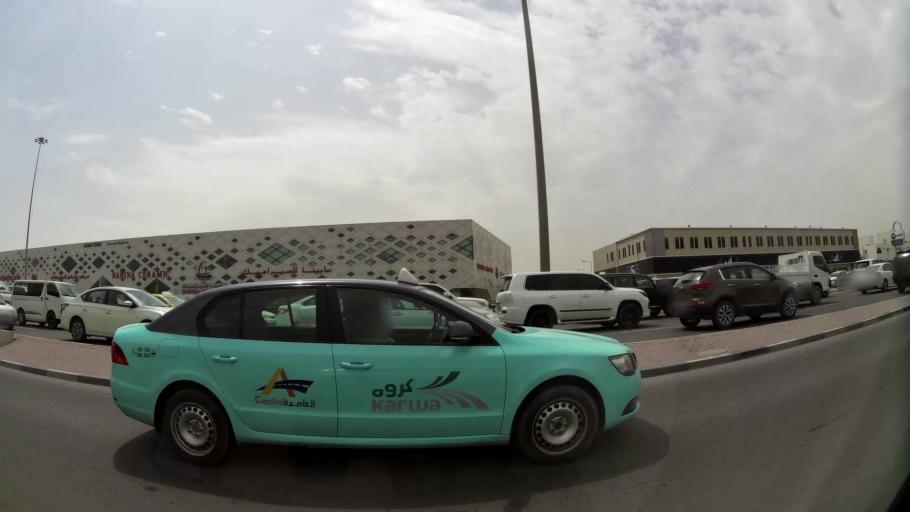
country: QA
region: Baladiyat ar Rayyan
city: Ar Rayyan
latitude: 25.3243
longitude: 51.4684
